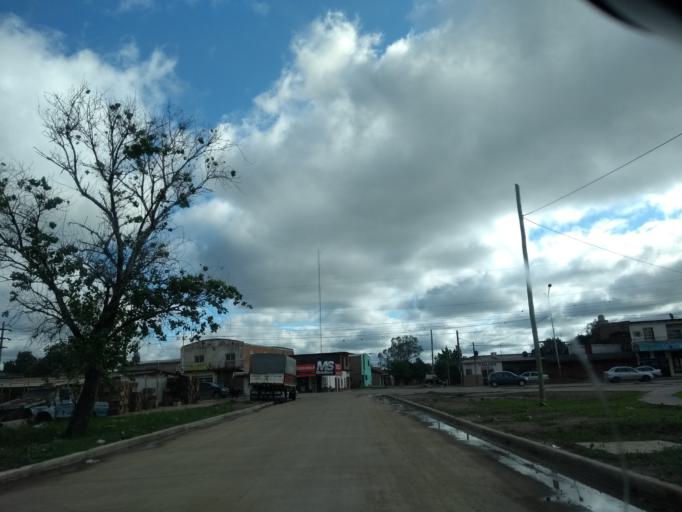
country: AR
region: Chaco
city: Resistencia
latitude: -27.4747
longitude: -58.9734
